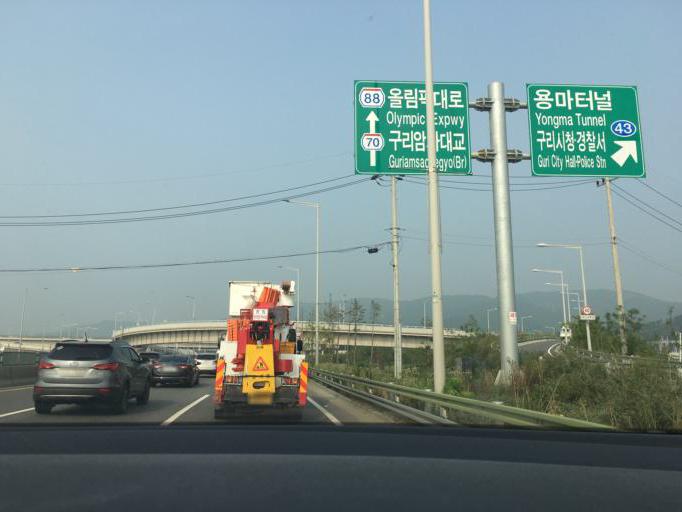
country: KR
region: Gyeonggi-do
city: Guri-si
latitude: 37.5746
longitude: 127.1317
